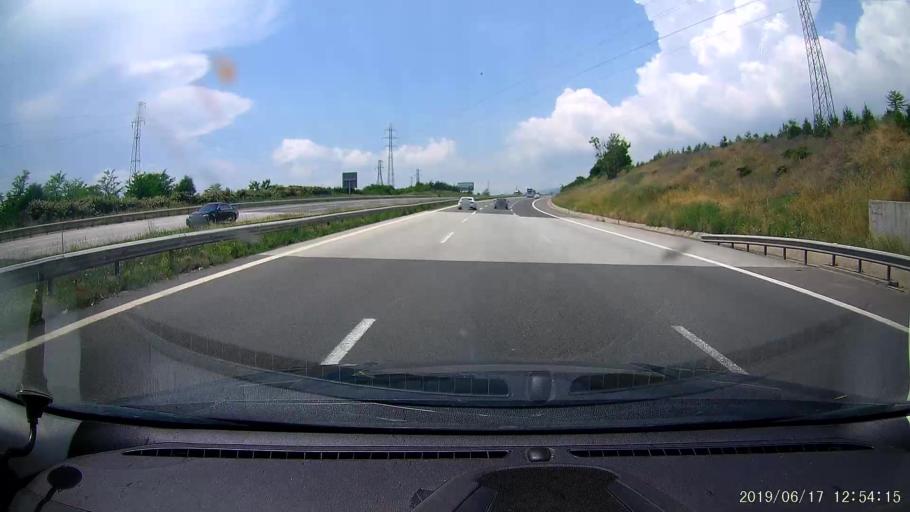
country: TR
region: Bolu
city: Bolu
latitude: 40.7660
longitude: 31.6270
